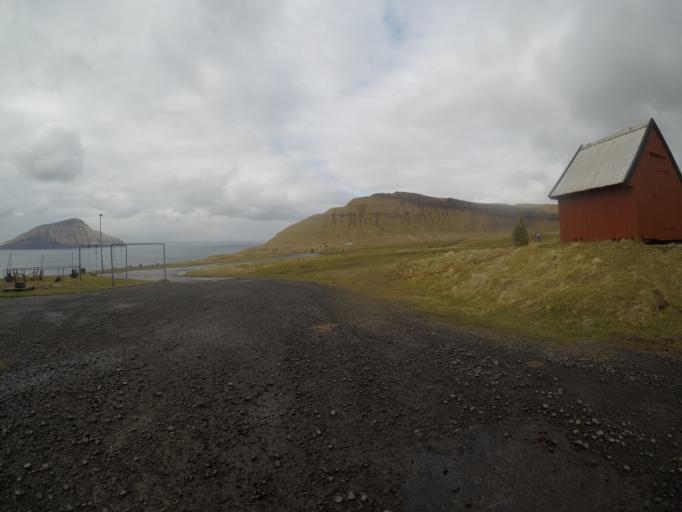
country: FO
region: Streymoy
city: Kollafjordhur
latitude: 62.0417
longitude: -6.9541
